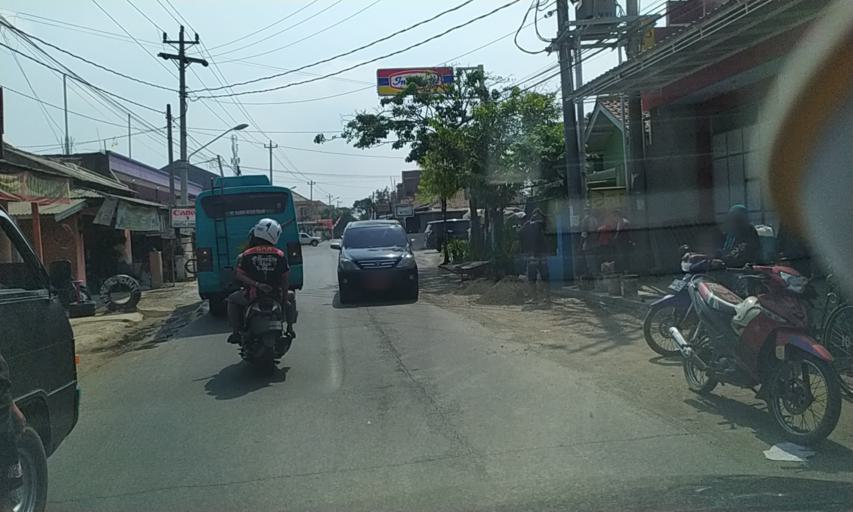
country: ID
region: Central Java
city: Tanjungsari
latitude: -7.3012
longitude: 108.7651
